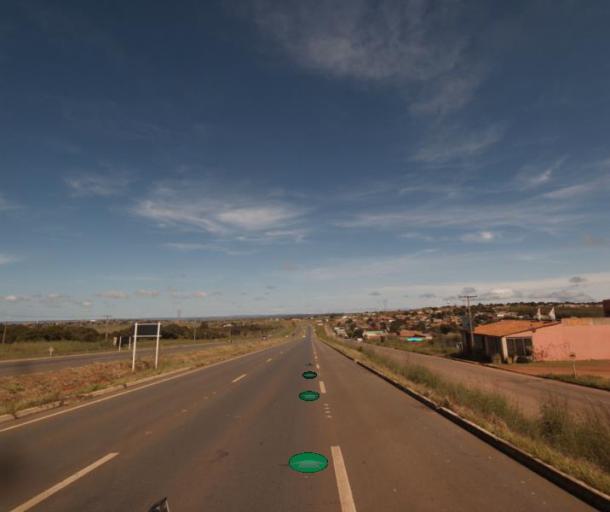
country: BR
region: Federal District
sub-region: Brasilia
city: Brasilia
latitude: -15.7393
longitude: -48.3041
